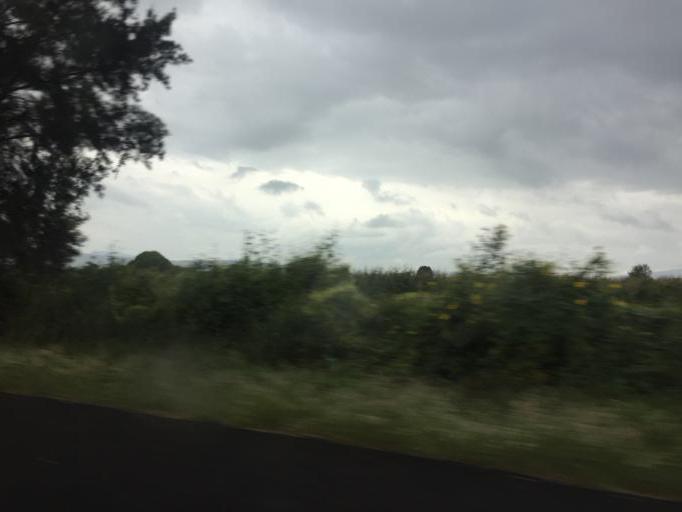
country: MX
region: Jalisco
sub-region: Zapotlan del Rey
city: Zapotlan del Rey
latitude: 20.4582
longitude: -102.8960
